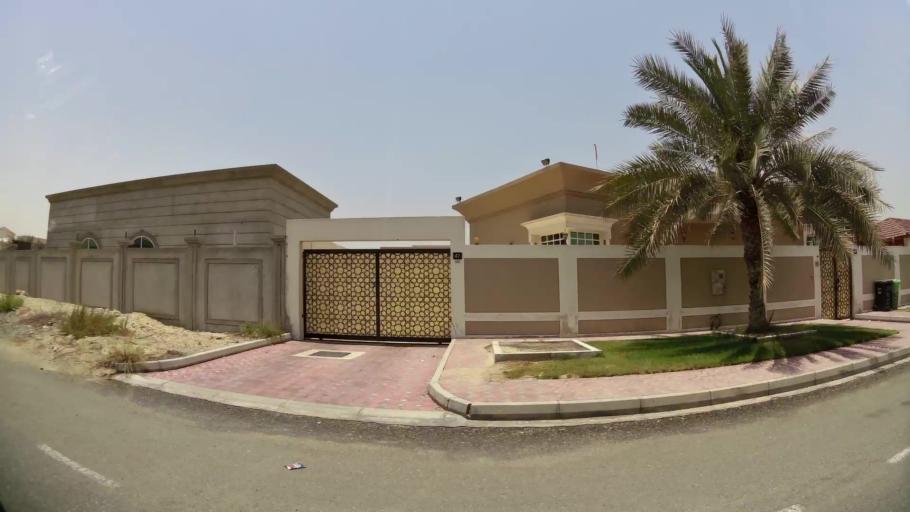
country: AE
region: Ash Shariqah
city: Sharjah
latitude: 25.2099
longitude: 55.3873
